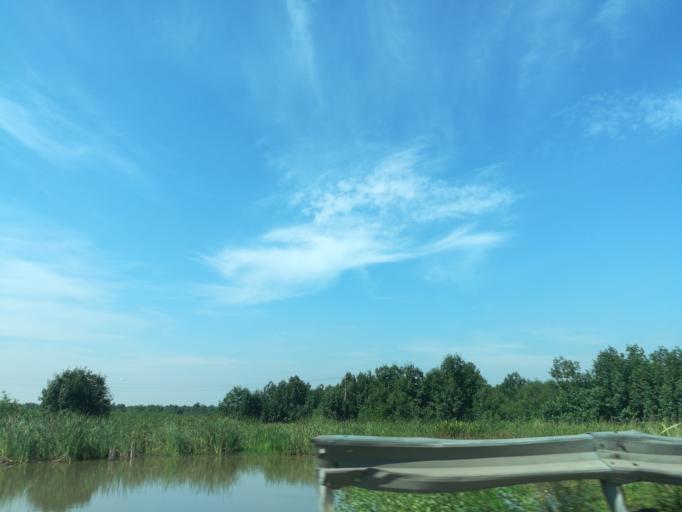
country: NG
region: Lagos
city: Ebute Ikorodu
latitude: 6.6194
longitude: 3.4585
